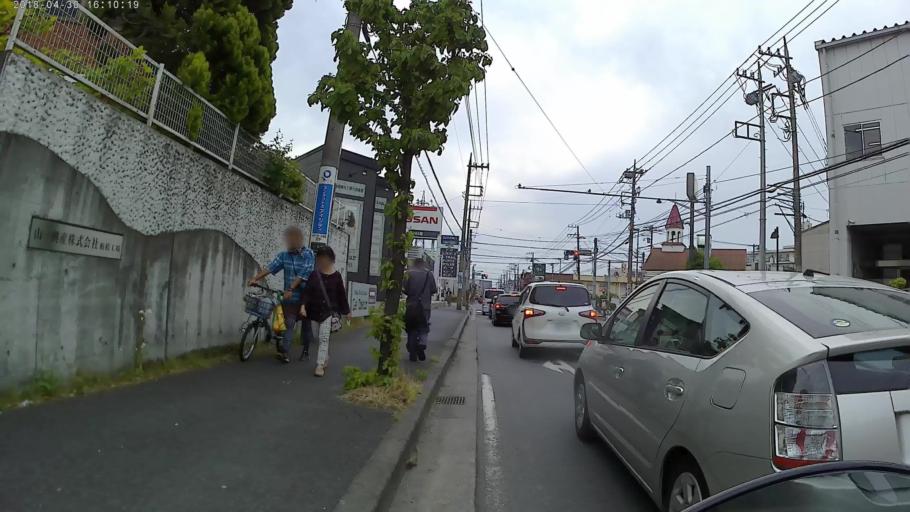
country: JP
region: Kanagawa
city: Minami-rinkan
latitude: 35.5016
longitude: 139.4290
